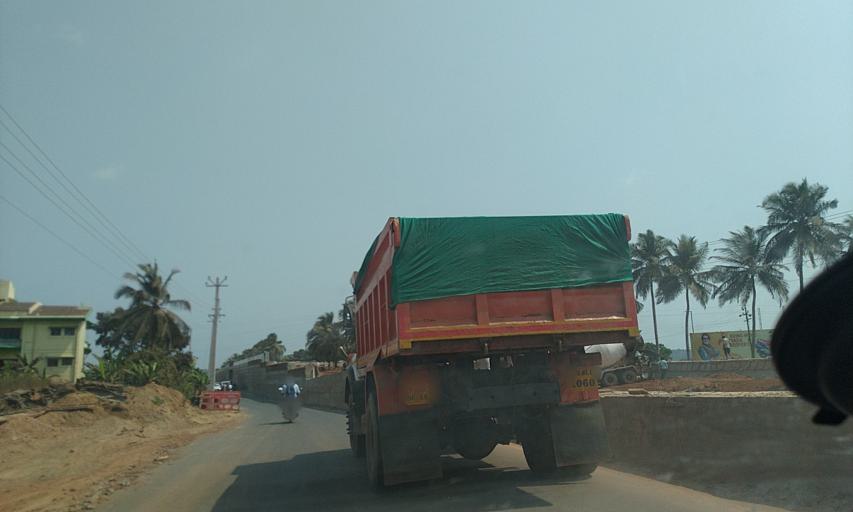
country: IN
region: Goa
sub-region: North Goa
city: Guirim
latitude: 15.5667
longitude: 73.8079
